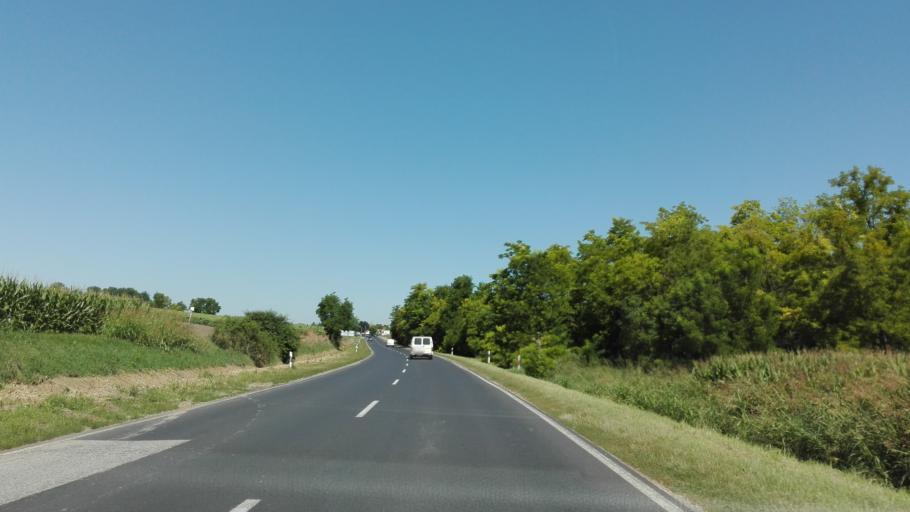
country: HU
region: Fejer
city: Mezoszilas
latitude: 46.8015
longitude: 18.4894
